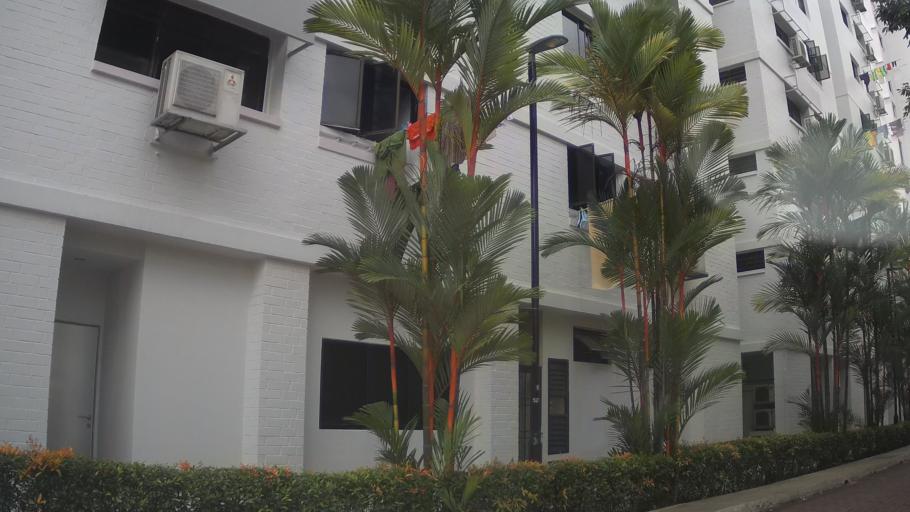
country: MY
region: Johor
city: Johor Bahru
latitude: 1.3857
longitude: 103.7652
